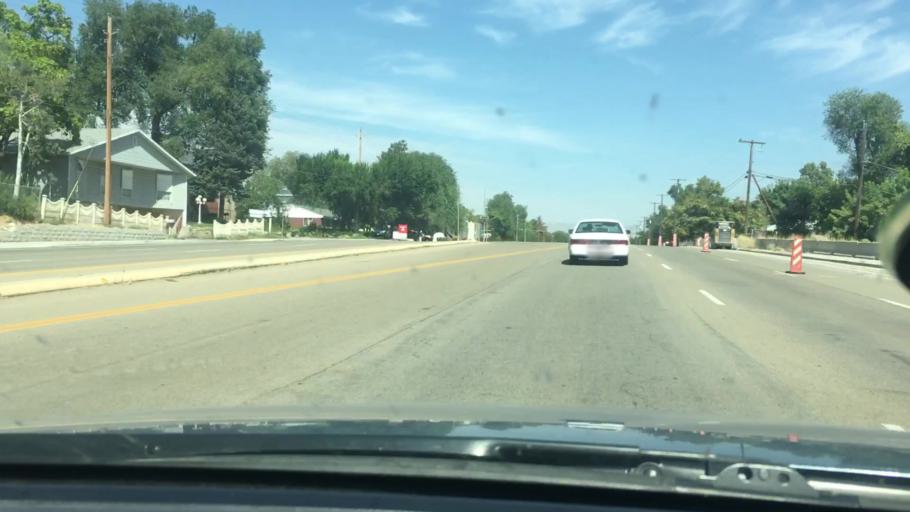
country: US
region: Utah
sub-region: Salt Lake County
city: Murray
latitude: 40.6702
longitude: -111.8714
